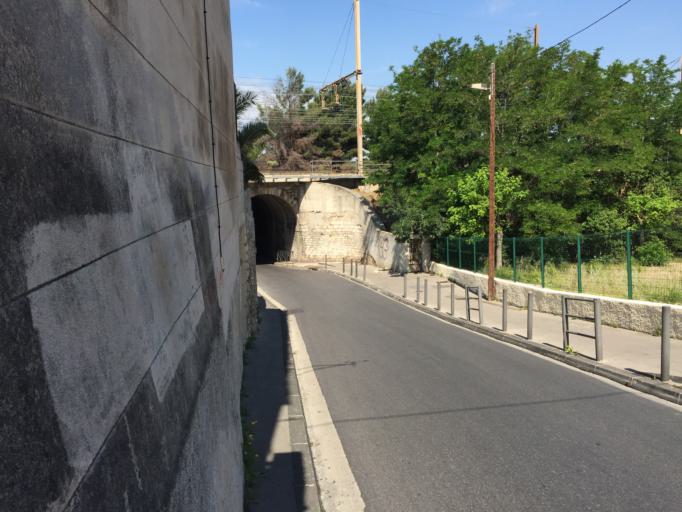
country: FR
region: Provence-Alpes-Cote d'Azur
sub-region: Departement des Bouches-du-Rhone
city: Marseille 04
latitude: 43.3141
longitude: 5.3941
